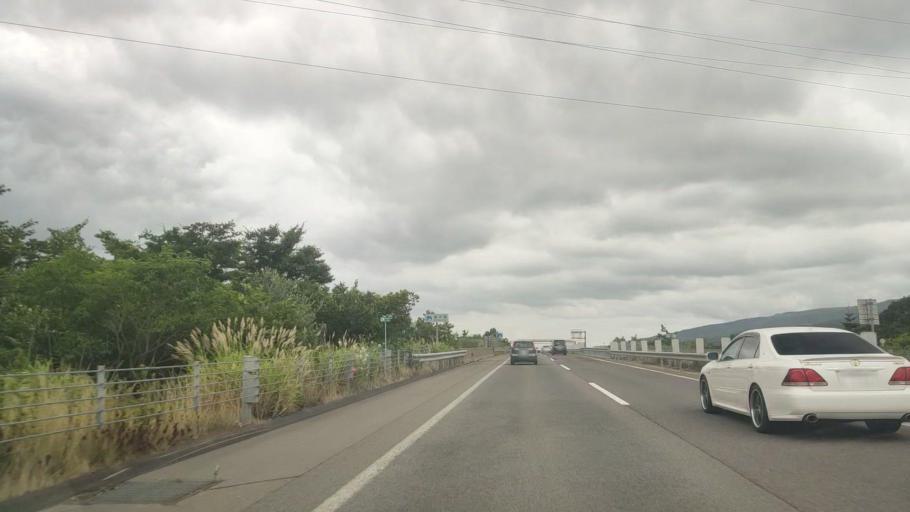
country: JP
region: Hokkaido
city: Nanae
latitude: 41.8585
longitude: 140.7355
